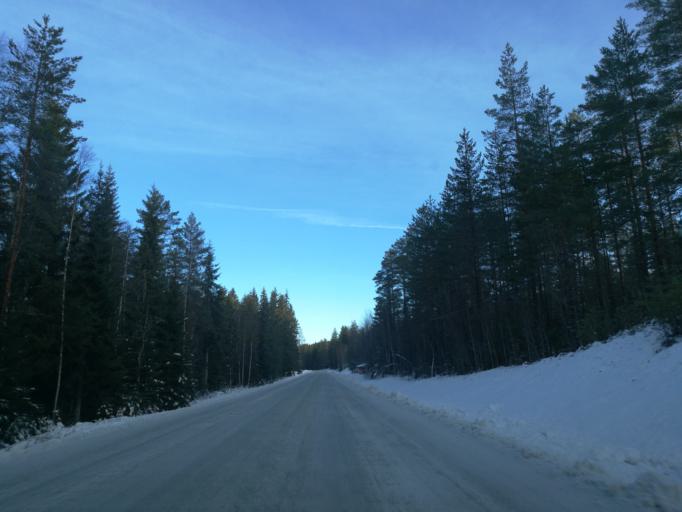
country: NO
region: Hedmark
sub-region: Grue
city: Kirkenaer
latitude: 60.3321
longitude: 12.2937
